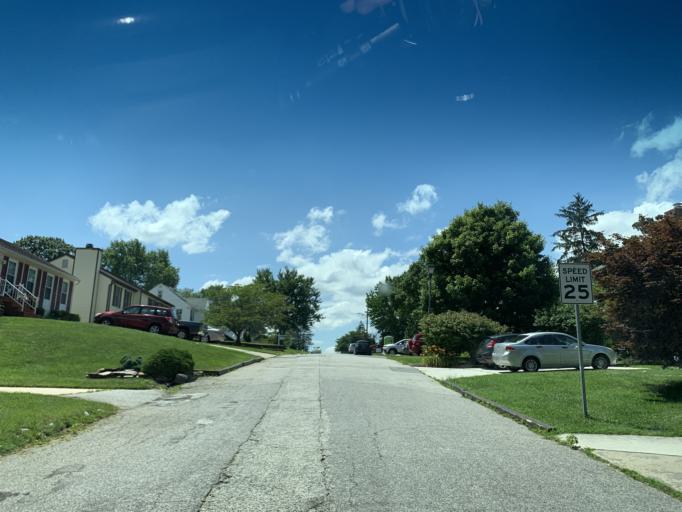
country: US
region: Maryland
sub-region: Baltimore County
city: Timonium
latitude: 39.4364
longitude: -76.6199
